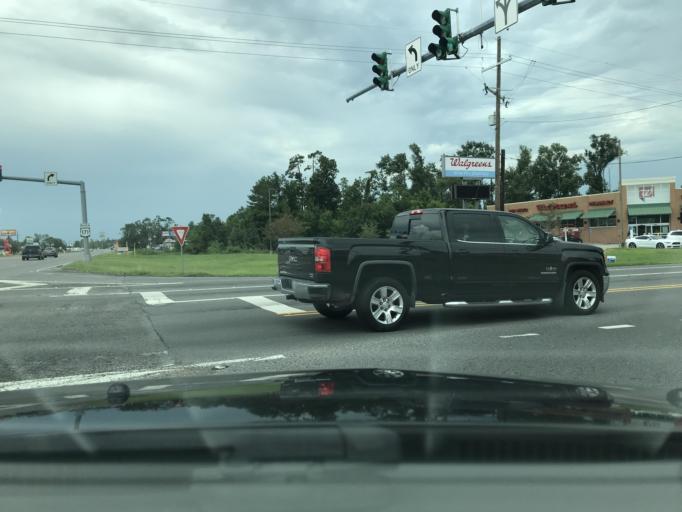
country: US
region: Louisiana
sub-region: Calcasieu Parish
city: Moss Bluff
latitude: 30.3005
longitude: -93.1951
